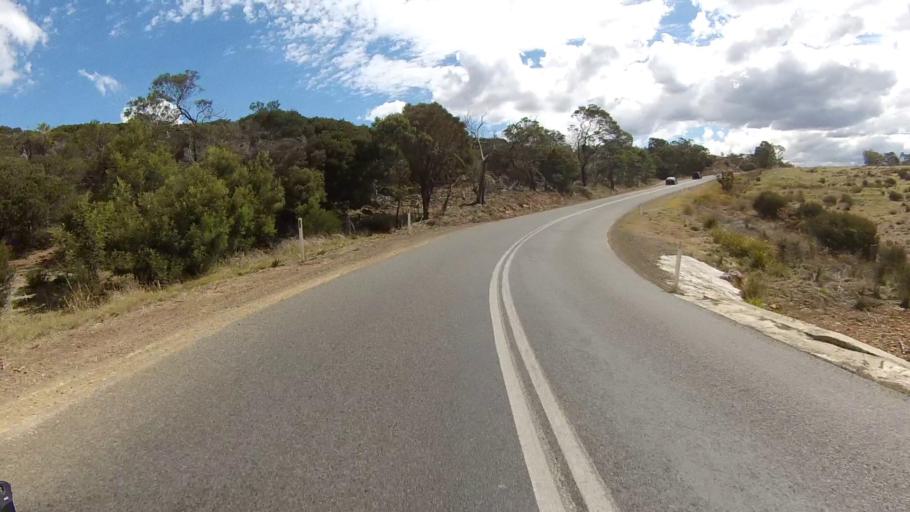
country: AU
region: Tasmania
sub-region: Break O'Day
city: St Helens
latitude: -41.9947
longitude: 148.1077
